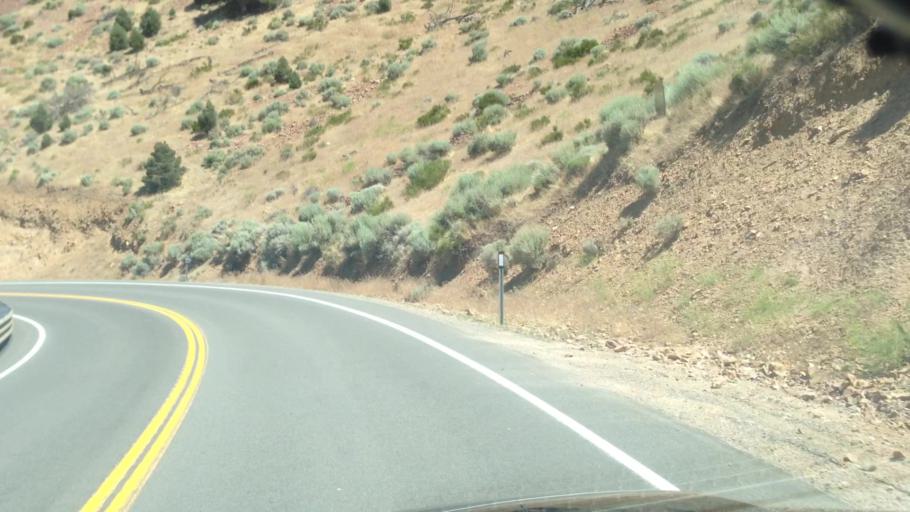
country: US
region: Nevada
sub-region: Storey County
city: Virginia City
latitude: 39.3824
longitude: -119.6967
